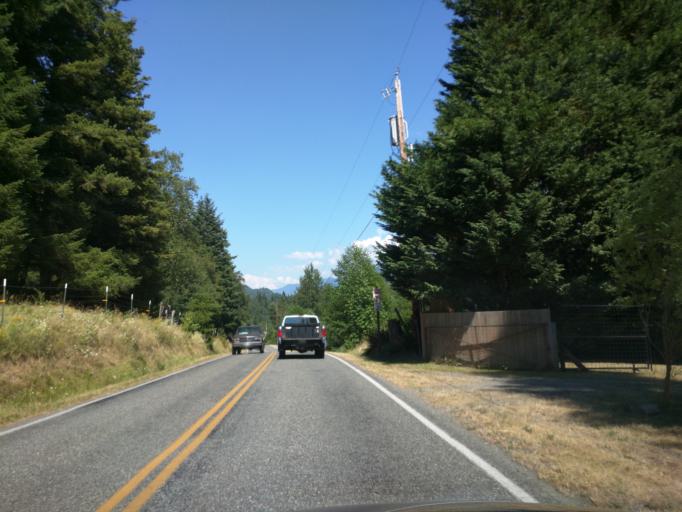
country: US
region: Washington
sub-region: Whatcom County
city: Sumas
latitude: 48.9479
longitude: -122.2262
